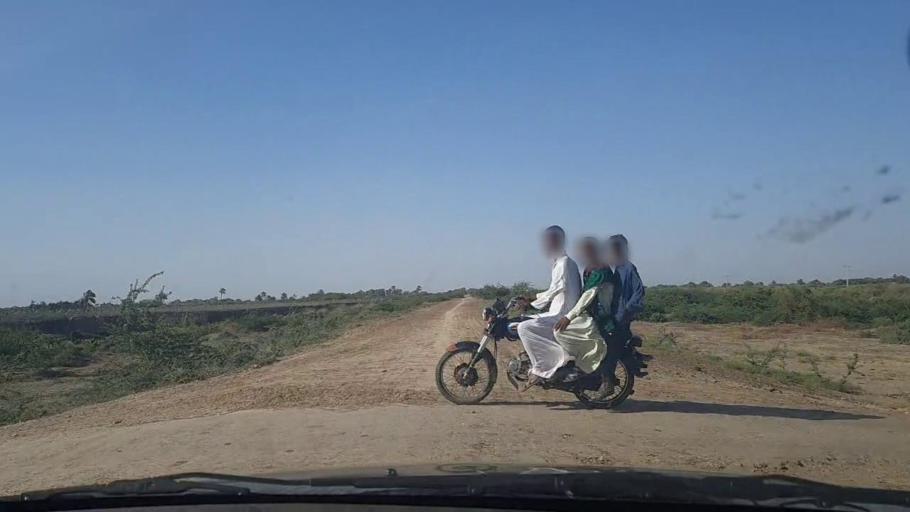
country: PK
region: Sindh
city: Chuhar Jamali
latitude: 24.3242
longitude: 67.7546
